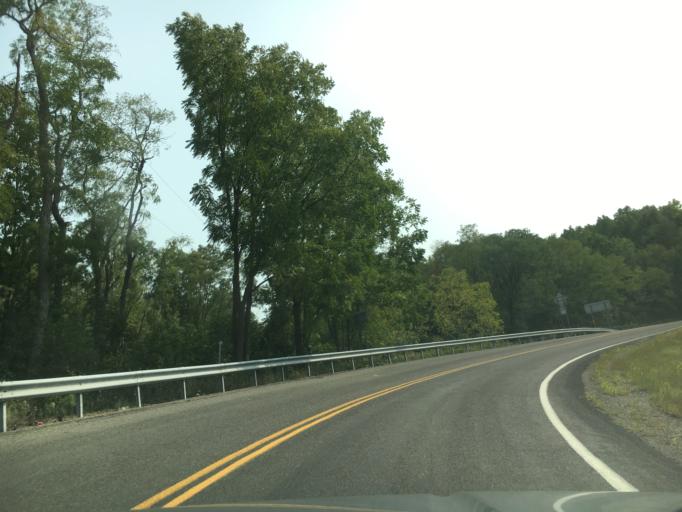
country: US
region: New York
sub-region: Steuben County
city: Sylvan Beach
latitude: 42.4875
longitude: -77.1259
